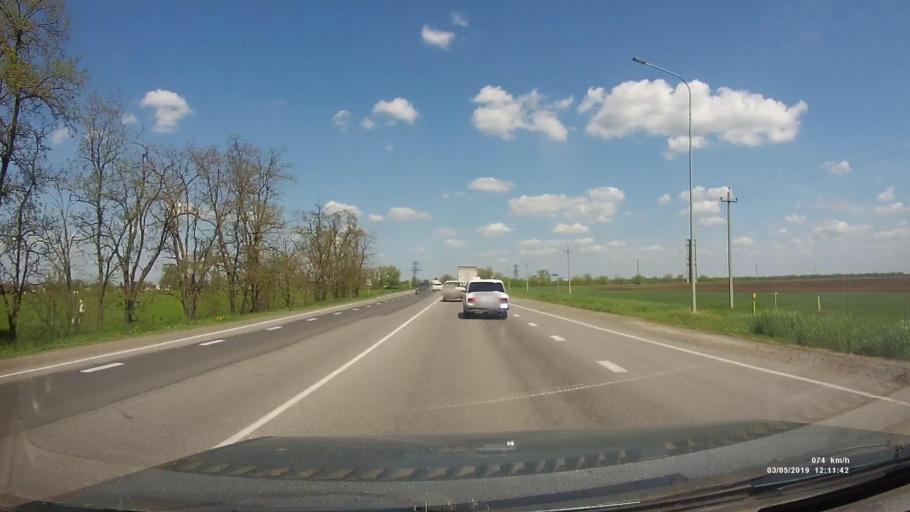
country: RU
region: Rostov
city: Bagayevskaya
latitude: 47.3134
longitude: 40.5406
